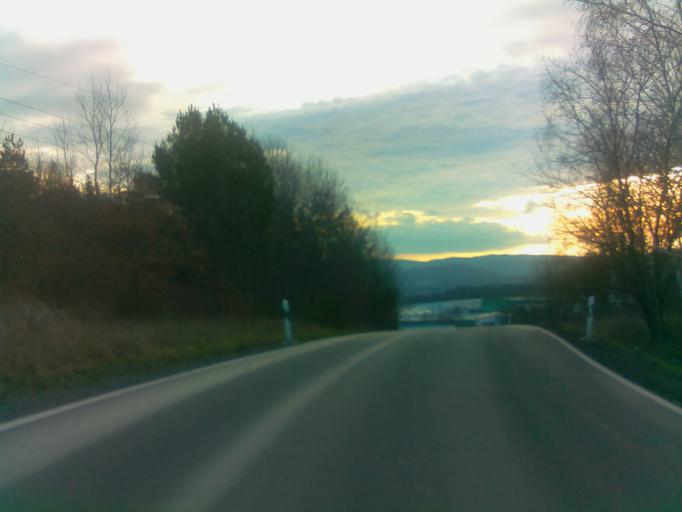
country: DE
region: Thuringia
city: Bad Blankenburg
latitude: 50.6594
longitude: 11.3140
